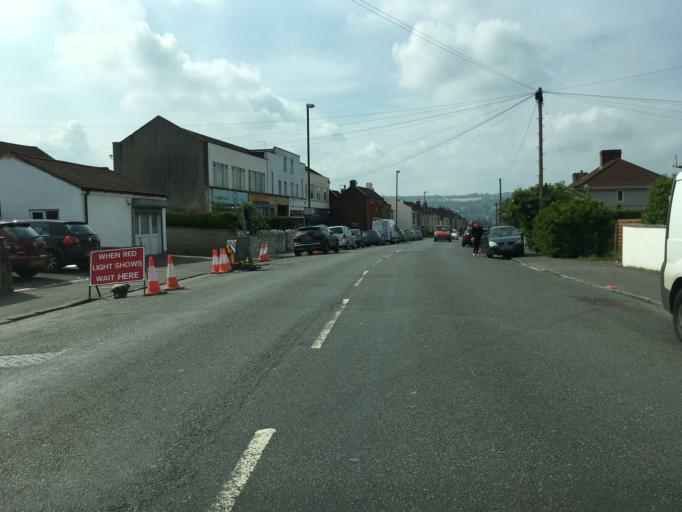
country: GB
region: England
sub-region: Bristol
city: Bristol
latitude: 51.4261
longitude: -2.6140
